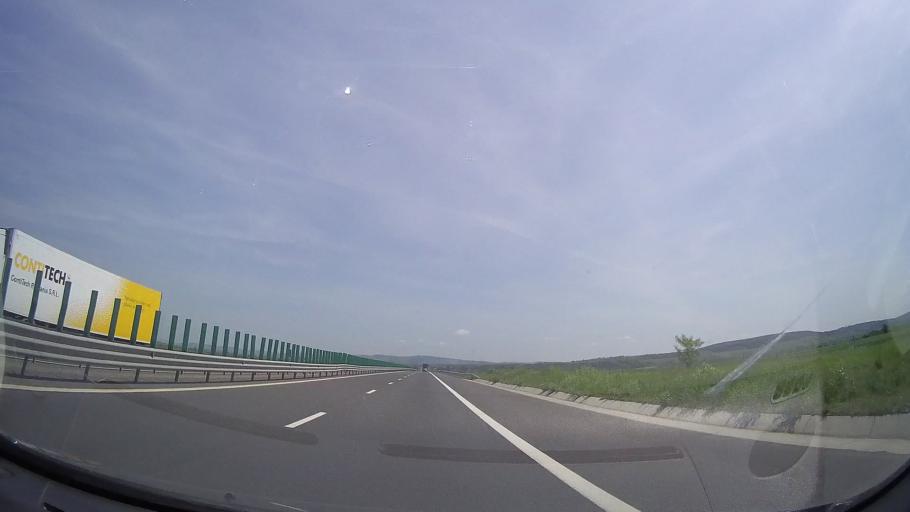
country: RO
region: Alba
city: Vurpar
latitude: 45.9612
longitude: 23.4546
